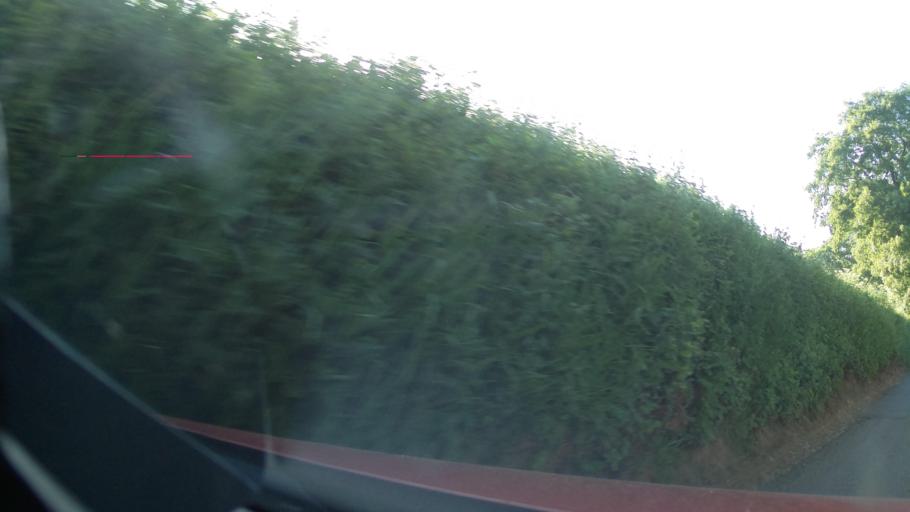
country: GB
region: England
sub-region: Devon
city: Topsham
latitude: 50.7236
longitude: -3.3960
